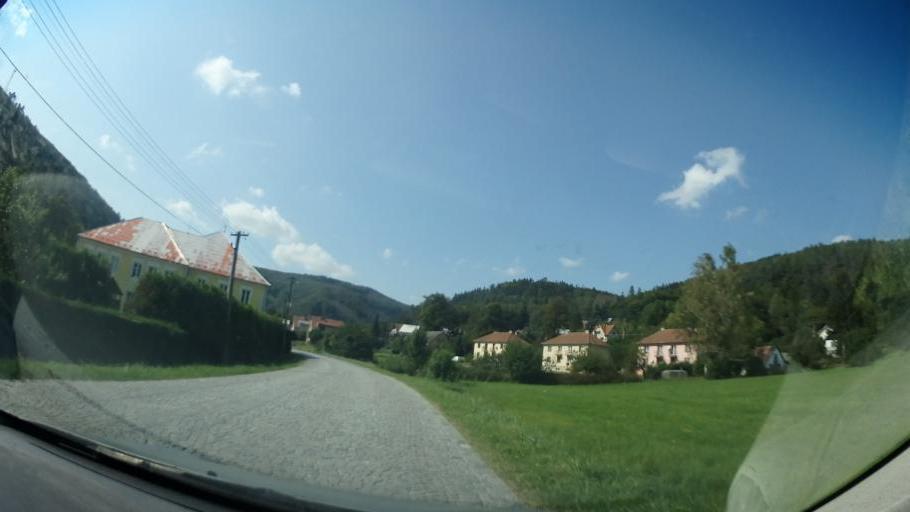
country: CZ
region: Vysocina
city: Bystrice nad Pernstejnem
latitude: 49.5573
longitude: 16.3246
